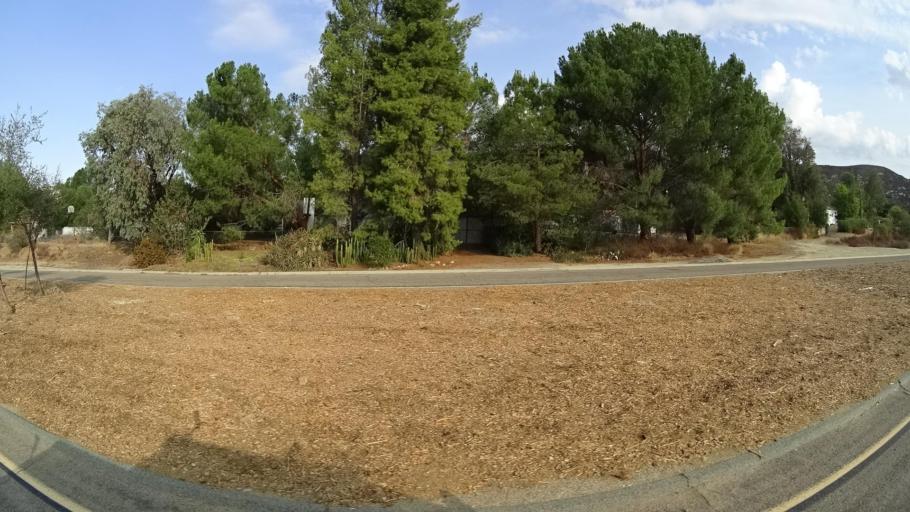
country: US
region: California
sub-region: San Diego County
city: San Diego Country Estates
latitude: 33.0237
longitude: -116.7999
